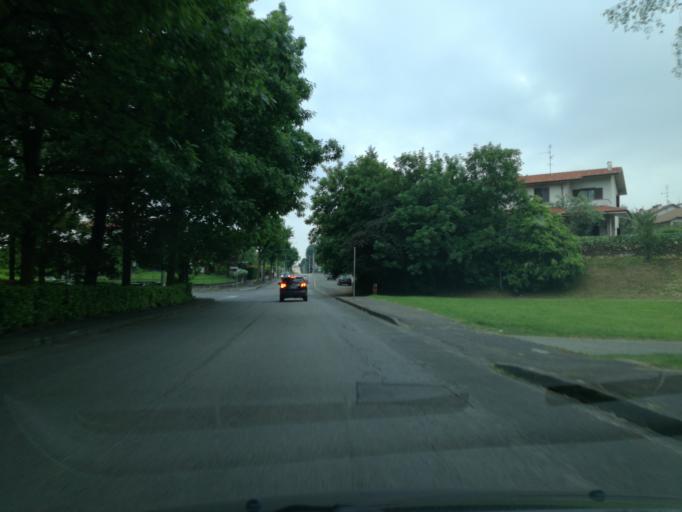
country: IT
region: Lombardy
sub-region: Provincia di Monza e Brianza
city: Carnate
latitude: 45.6484
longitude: 9.3750
